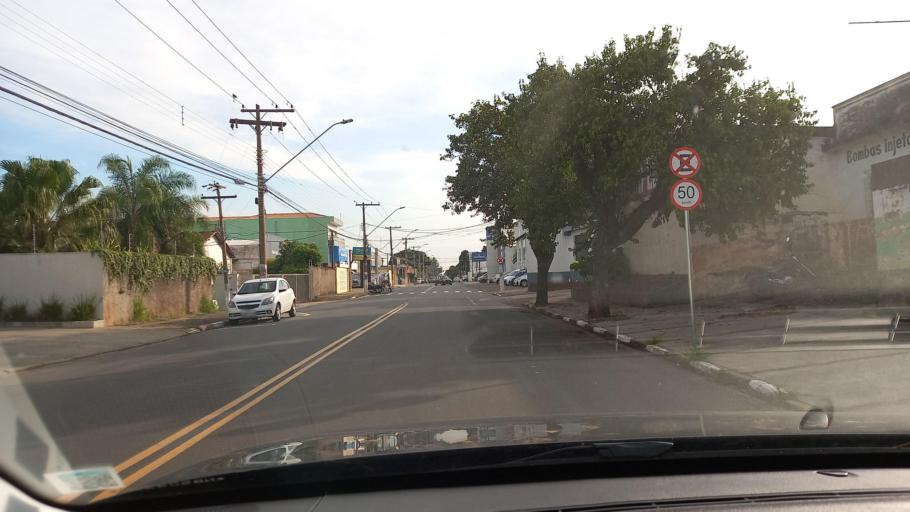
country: BR
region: Sao Paulo
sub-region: Mogi-Mirim
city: Mogi Mirim
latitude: -22.4424
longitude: -46.9698
